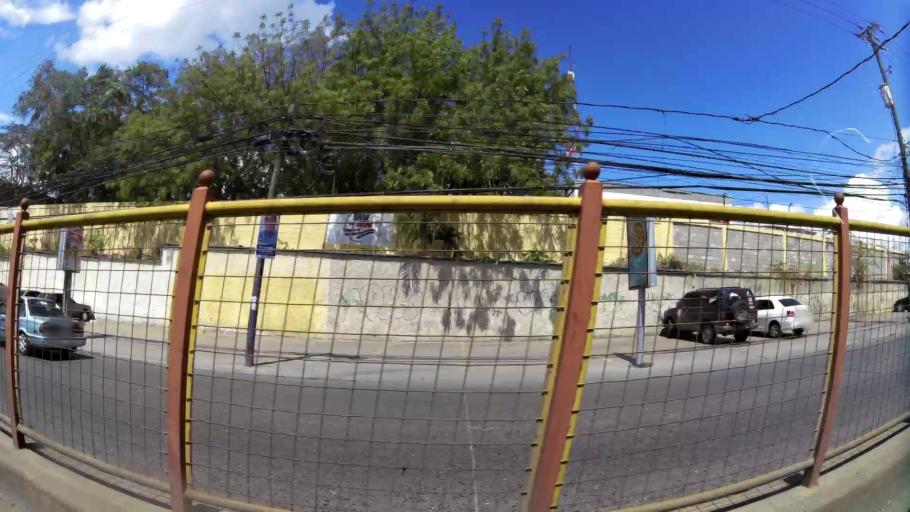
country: DO
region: Santiago
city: Santiago de los Caballeros
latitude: 19.4310
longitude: -70.6917
